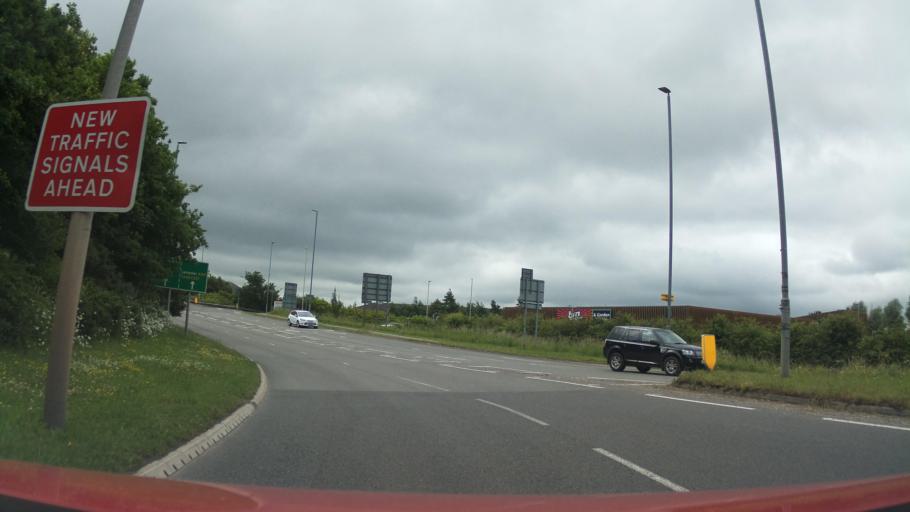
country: GB
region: England
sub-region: Leicestershire
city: Ashby de la Zouch
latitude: 52.7515
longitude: -1.4502
